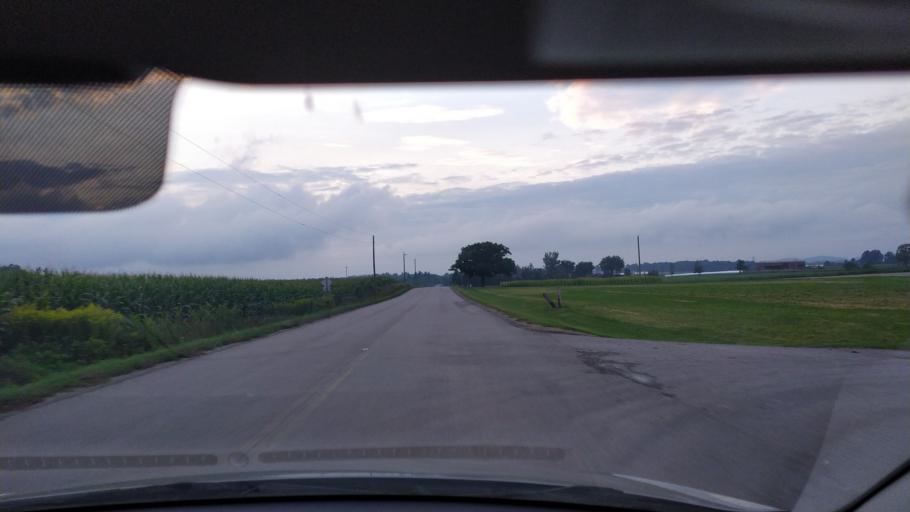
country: CA
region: Ontario
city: Kitchener
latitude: 43.3373
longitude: -80.6287
